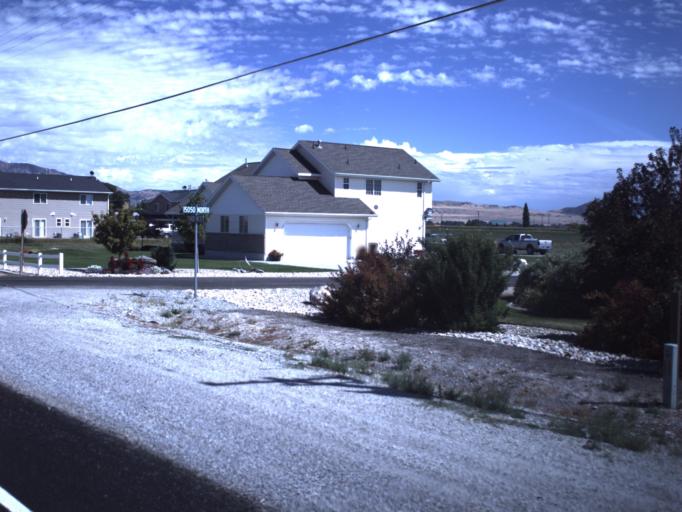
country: US
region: Utah
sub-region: Box Elder County
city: Garland
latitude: 41.7818
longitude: -112.1492
